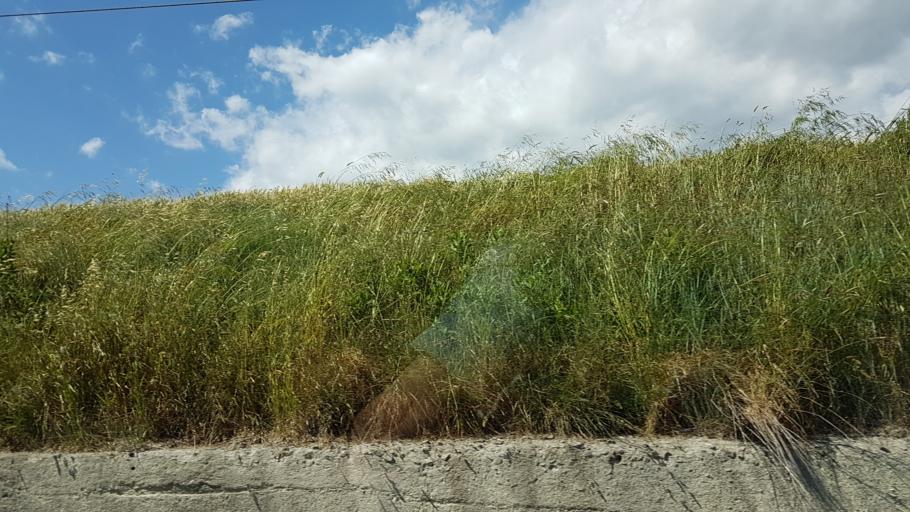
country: IT
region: Tuscany
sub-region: Province of Pisa
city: Orciano Pisano
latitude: 43.4520
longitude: 10.5153
